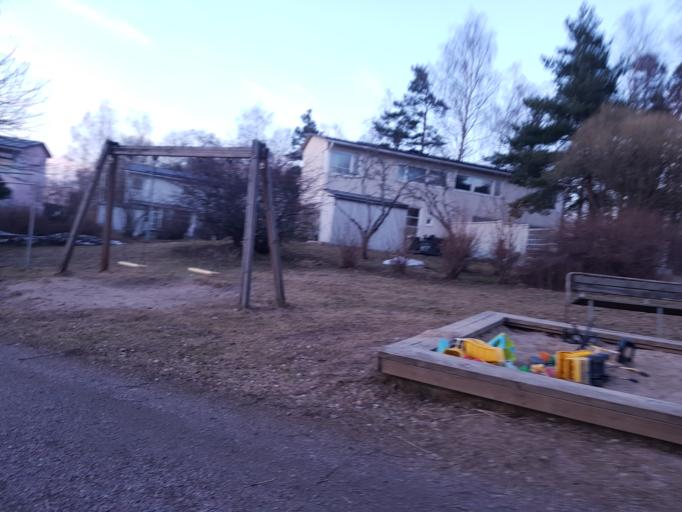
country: FI
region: Uusimaa
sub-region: Helsinki
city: Helsinki
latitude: 60.2596
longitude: 24.9467
